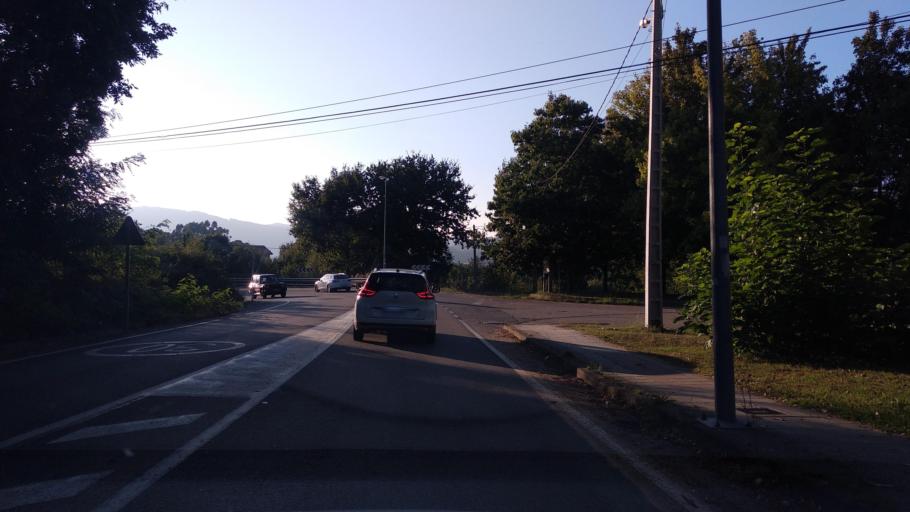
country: ES
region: Galicia
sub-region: Provincia de Pontevedra
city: Redondela
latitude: 42.3411
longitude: -8.5931
